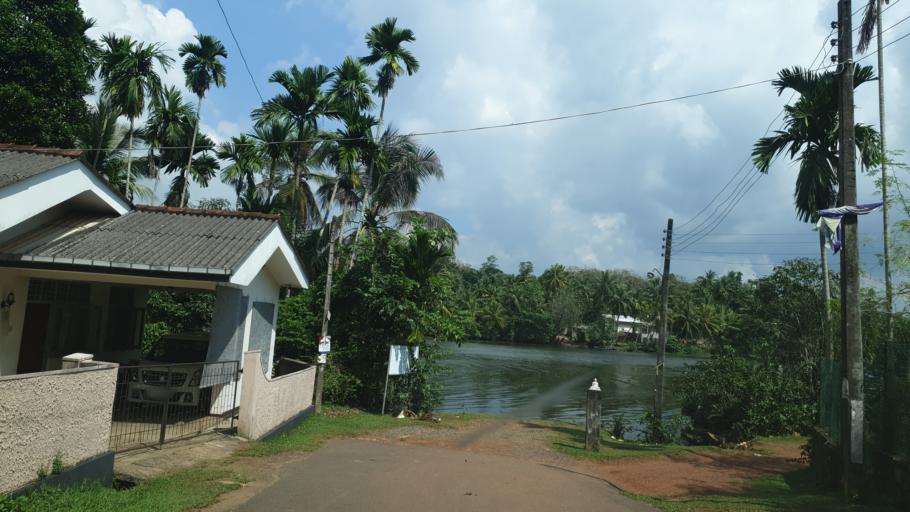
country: LK
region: Western
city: Panadura
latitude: 6.7239
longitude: 79.9650
